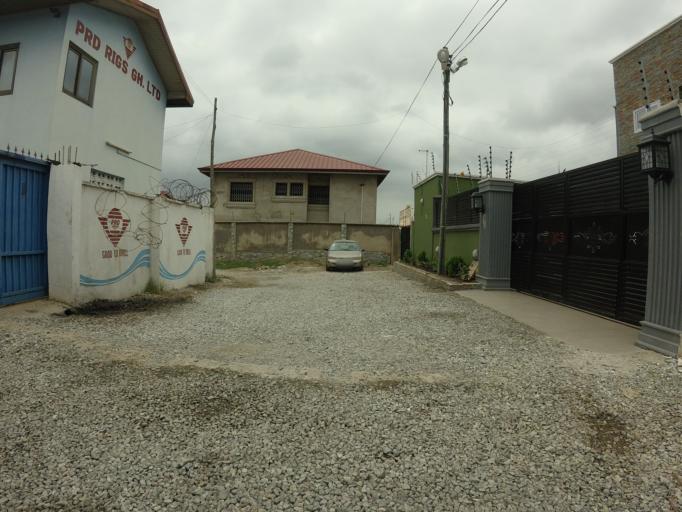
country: GH
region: Greater Accra
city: Dome
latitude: 5.6338
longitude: -0.2379
